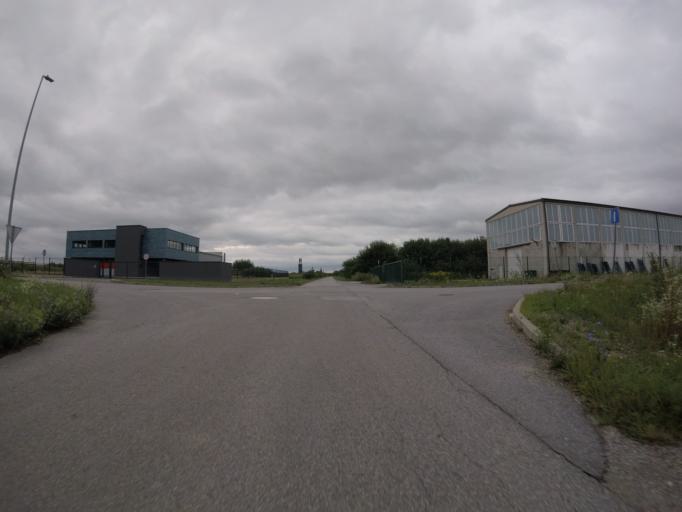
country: HR
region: Zagrebacka
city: Turopolje
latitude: 45.6555
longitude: 16.1278
